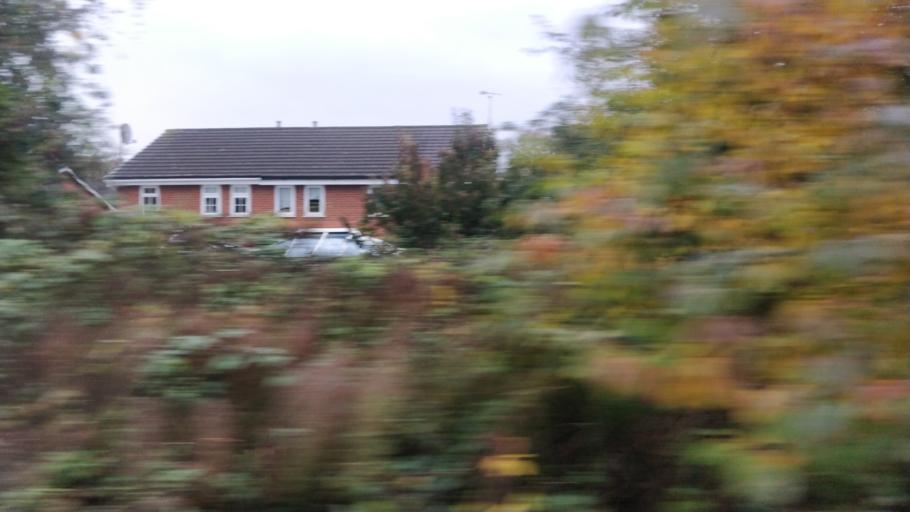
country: GB
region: England
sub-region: Lancashire
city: Appley Bridge
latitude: 53.5771
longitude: -2.7158
